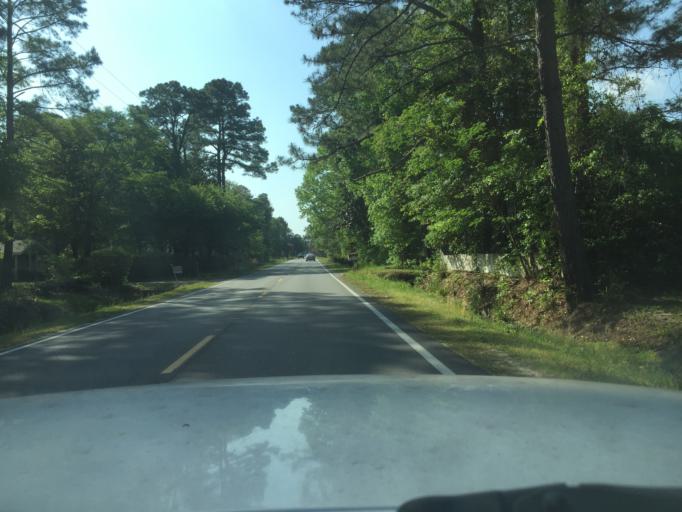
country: US
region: Georgia
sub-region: Chatham County
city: Georgetown
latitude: 32.0275
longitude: -81.2190
